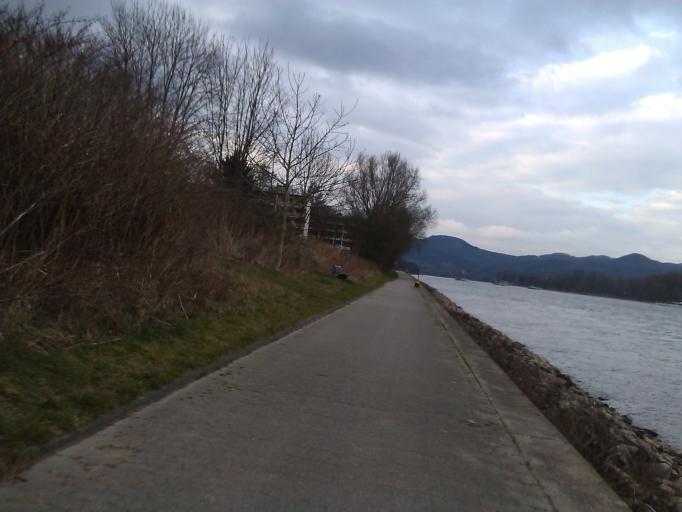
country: DE
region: North Rhine-Westphalia
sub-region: Regierungsbezirk Koln
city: Bad Honnef
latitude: 50.6263
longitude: 7.2097
